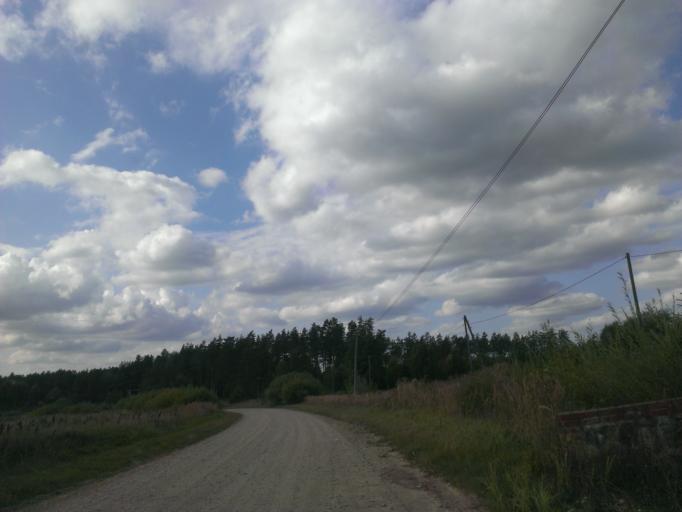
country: LV
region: Incukalns
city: Vangazi
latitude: 57.1201
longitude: 24.5686
